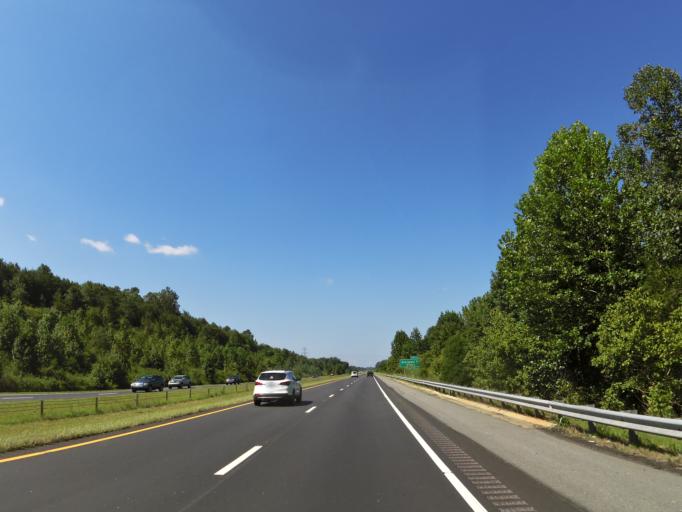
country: US
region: North Carolina
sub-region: Catawba County
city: Maiden
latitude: 35.5619
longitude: -81.2479
